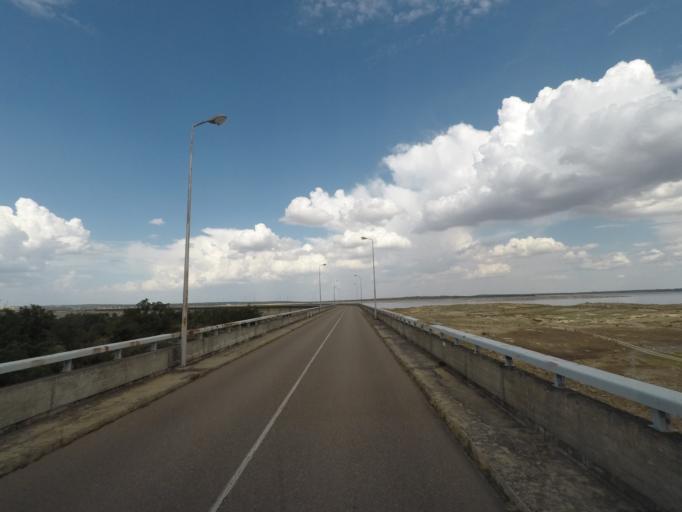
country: ES
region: Castille and Leon
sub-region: Provincia de Salamanca
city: Almendra
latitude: 41.2585
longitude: -6.3237
